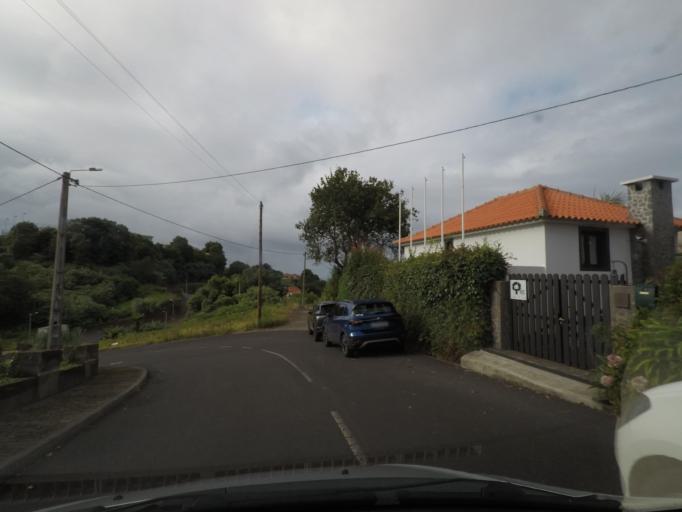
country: PT
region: Madeira
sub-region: Santana
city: Santana
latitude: 32.8022
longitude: -16.8739
